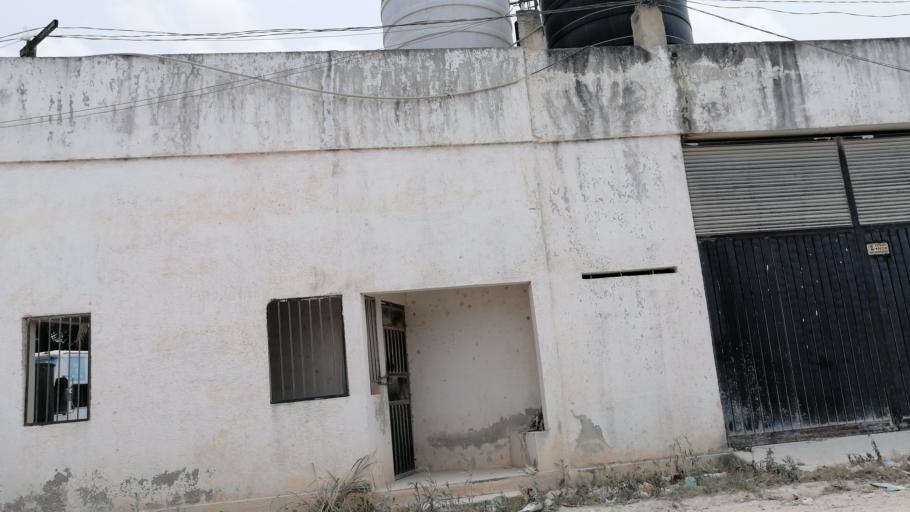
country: MX
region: Quintana Roo
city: Cancun
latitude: 21.1375
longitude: -86.8976
